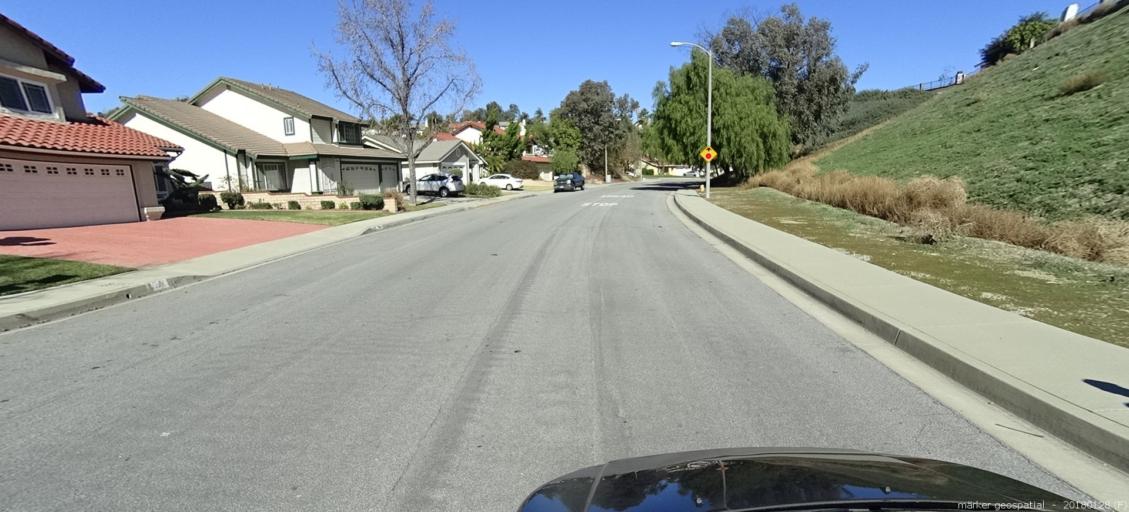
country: US
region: California
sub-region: San Bernardino County
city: Chino Hills
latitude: 33.9961
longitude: -117.7919
